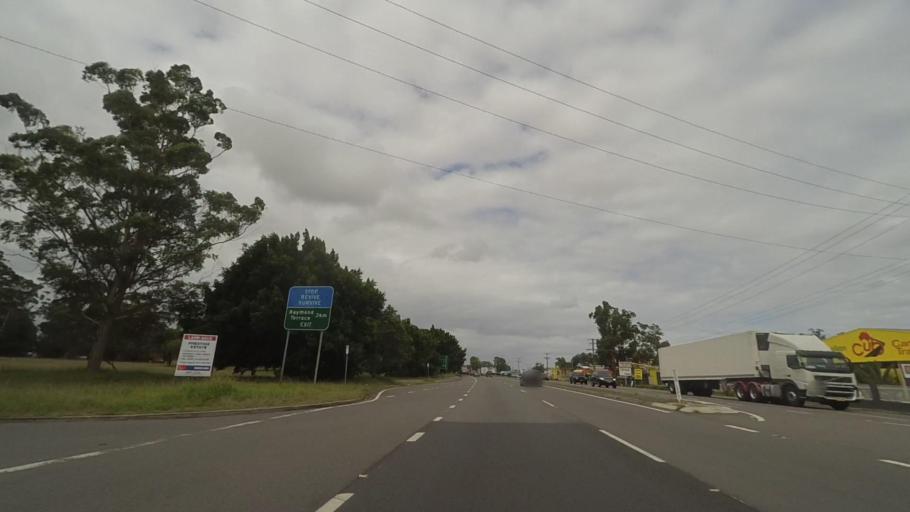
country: AU
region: New South Wales
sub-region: Port Stephens Shire
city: Raymond Terrace
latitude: -32.7874
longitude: 151.7293
